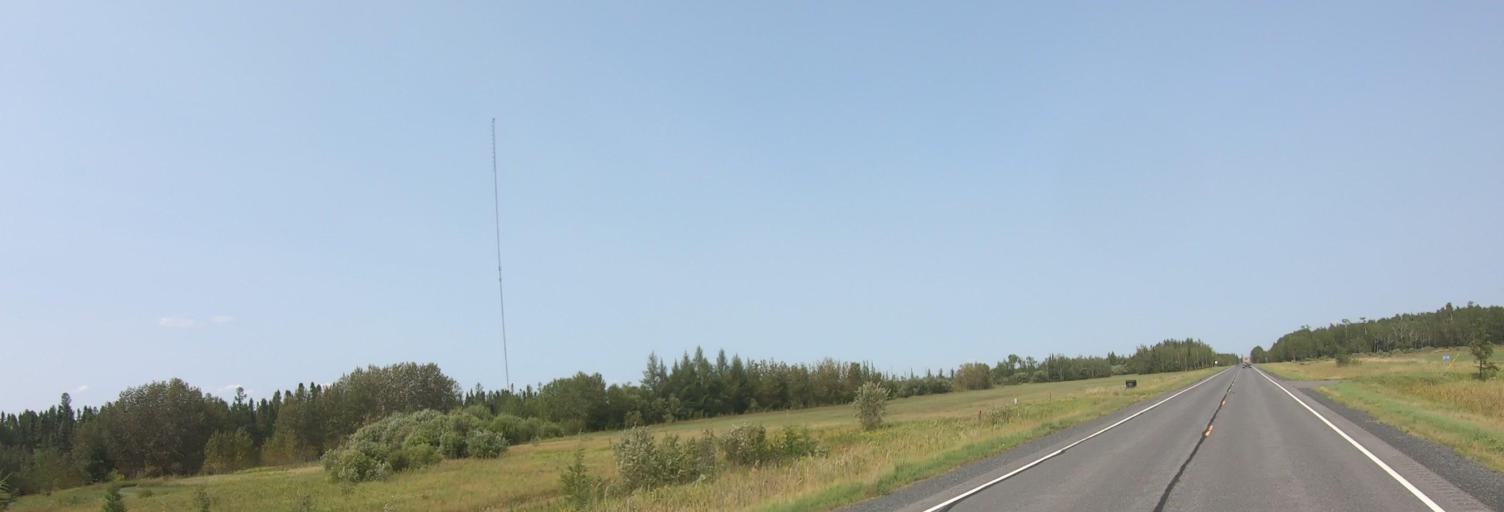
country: US
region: Minnesota
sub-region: Koochiching County
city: International Falls
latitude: 48.5597
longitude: -93.8182
